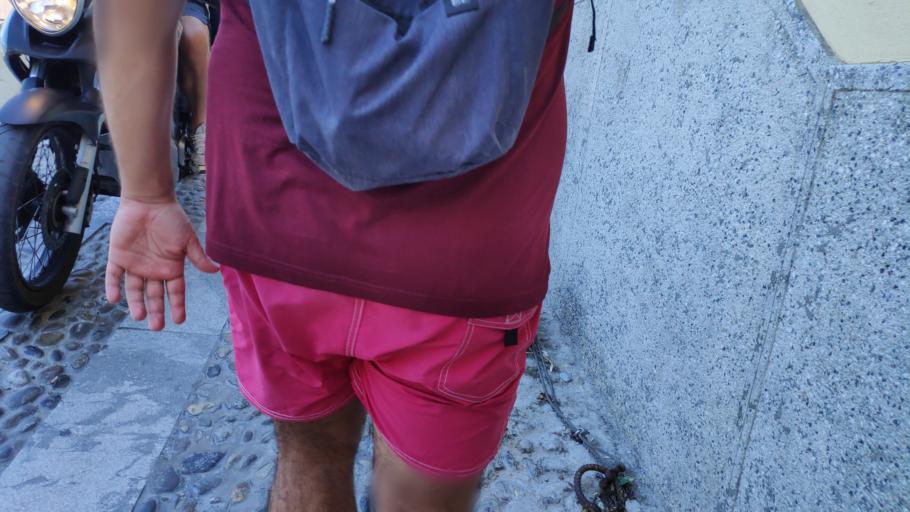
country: IT
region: Calabria
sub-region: Provincia di Reggio Calabria
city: Scilla
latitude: 38.2542
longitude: 15.7175
